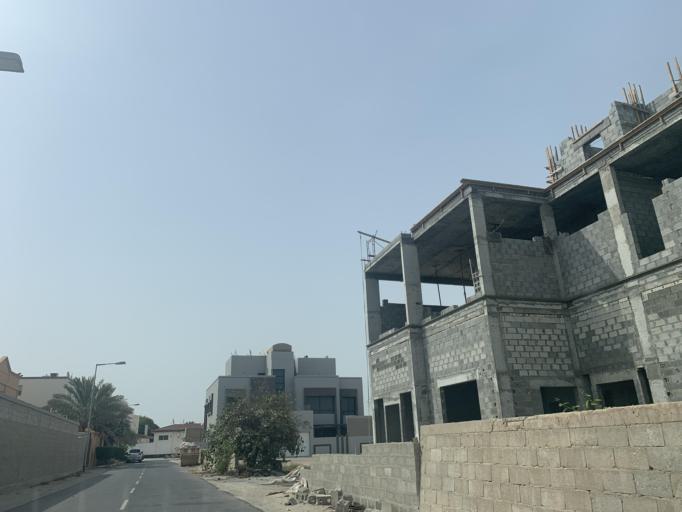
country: BH
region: Manama
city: Jidd Hafs
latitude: 26.1999
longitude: 50.4816
